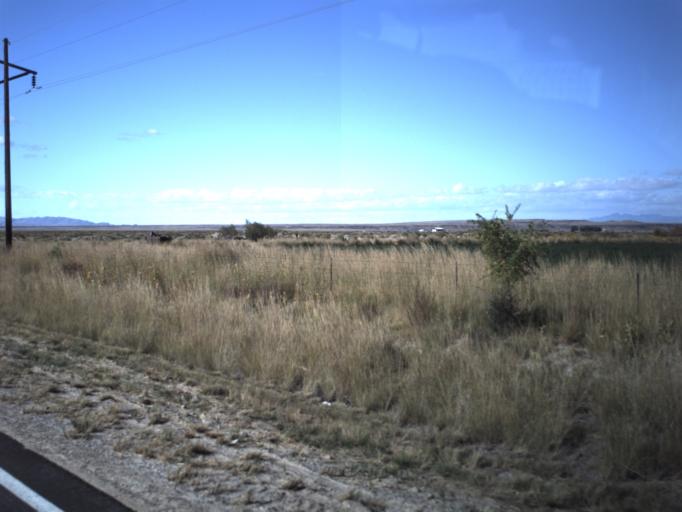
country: US
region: Utah
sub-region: Millard County
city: Delta
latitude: 39.2445
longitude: -112.6603
